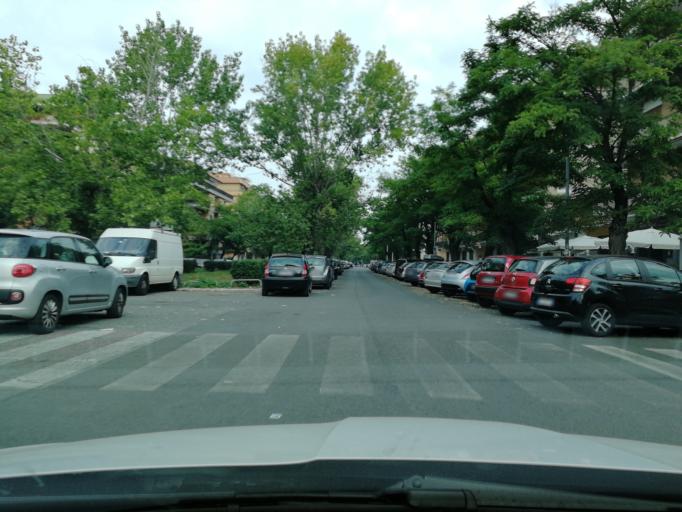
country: IT
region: Latium
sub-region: Citta metropolitana di Roma Capitale
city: Rome
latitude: 41.8506
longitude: 12.5639
